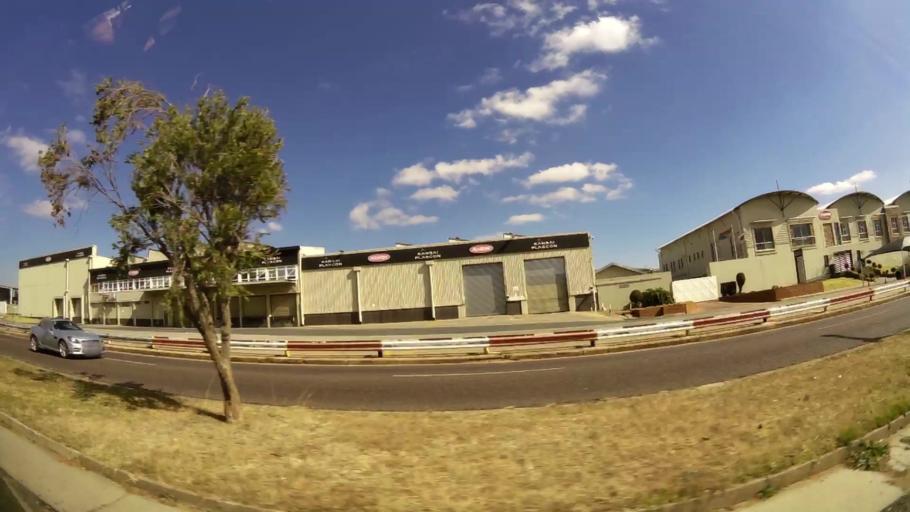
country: ZA
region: Gauteng
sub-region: West Rand District Municipality
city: Krugersdorp
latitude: -26.1175
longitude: 27.8173
